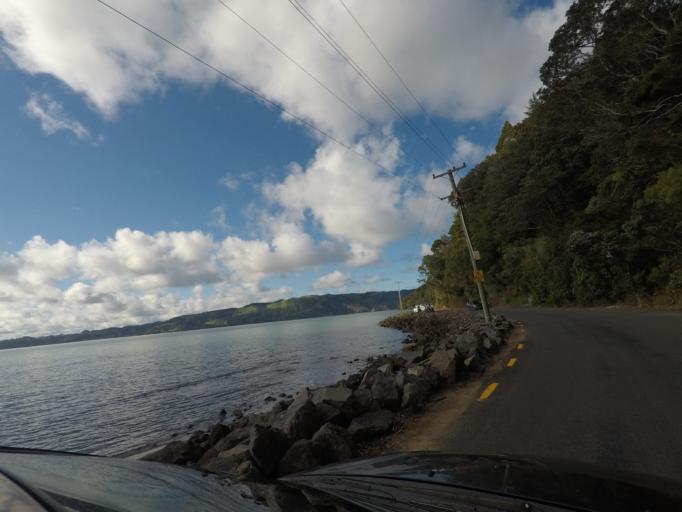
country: NZ
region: Auckland
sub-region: Auckland
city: Titirangi
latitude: -37.0109
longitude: 174.5621
